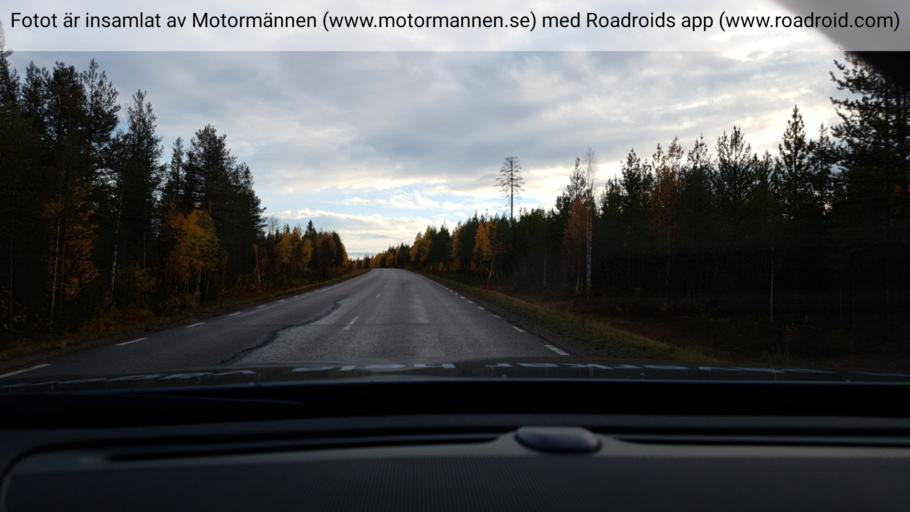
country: SE
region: Norrbotten
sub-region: Overkalix Kommun
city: OEverkalix
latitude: 66.8660
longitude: 22.7554
